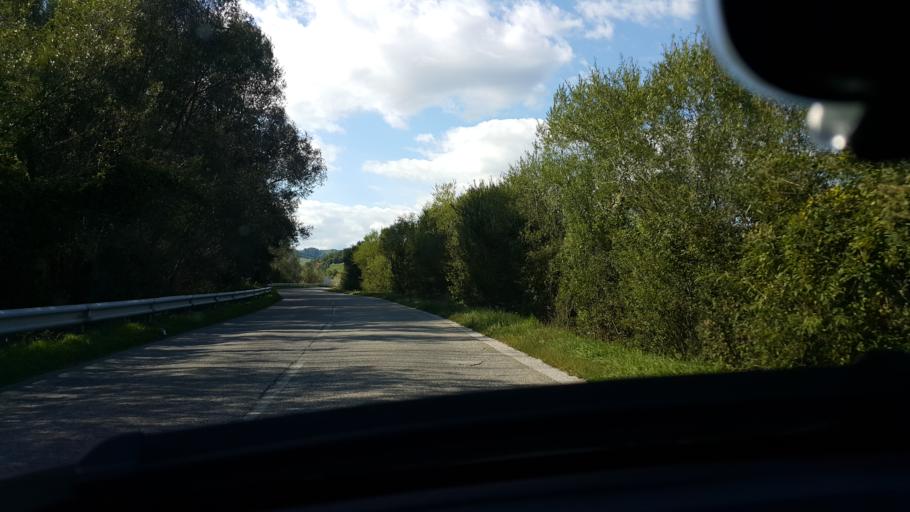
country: SI
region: Pesnica
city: Pesnica pri Mariboru
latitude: 46.6028
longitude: 15.6677
